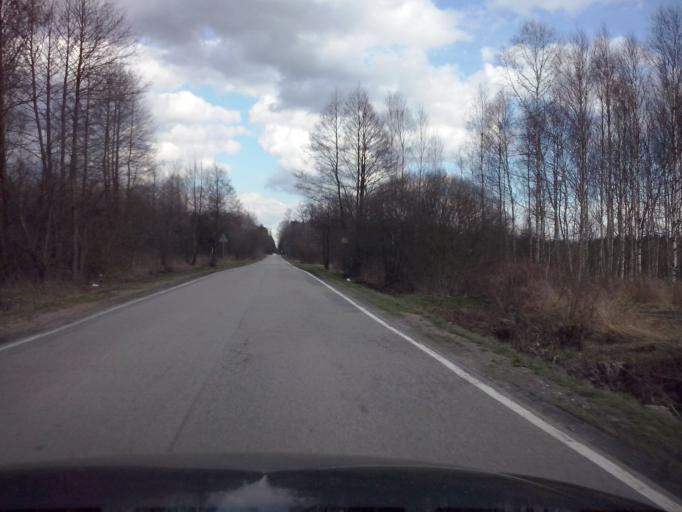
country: PL
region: Subcarpathian Voivodeship
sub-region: Powiat nizanski
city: Harasiuki
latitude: 50.5028
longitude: 22.5448
